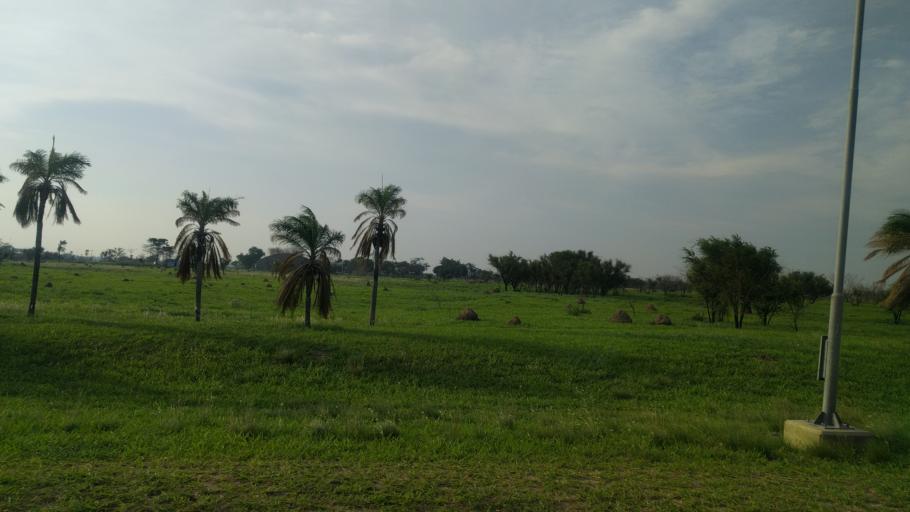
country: BO
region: Santa Cruz
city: La Belgica
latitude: -17.6501
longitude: -63.1452
